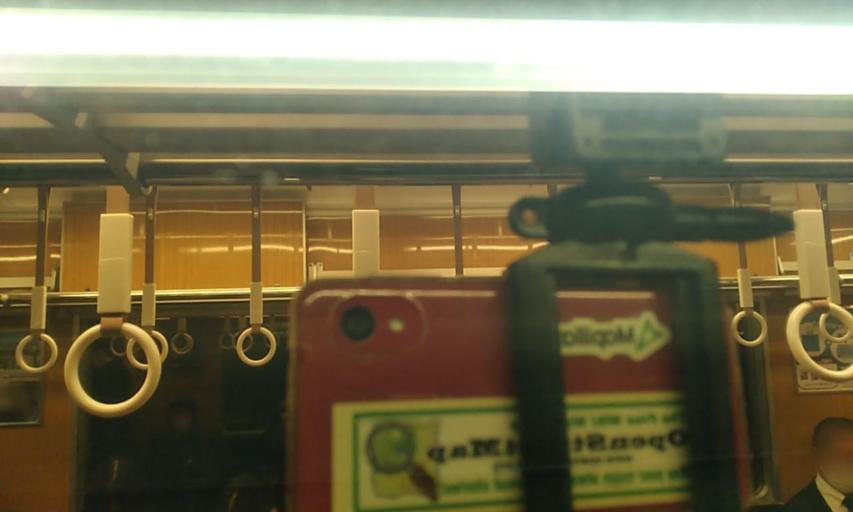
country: JP
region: Kyoto
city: Kyoto
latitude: 35.0027
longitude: 135.7299
